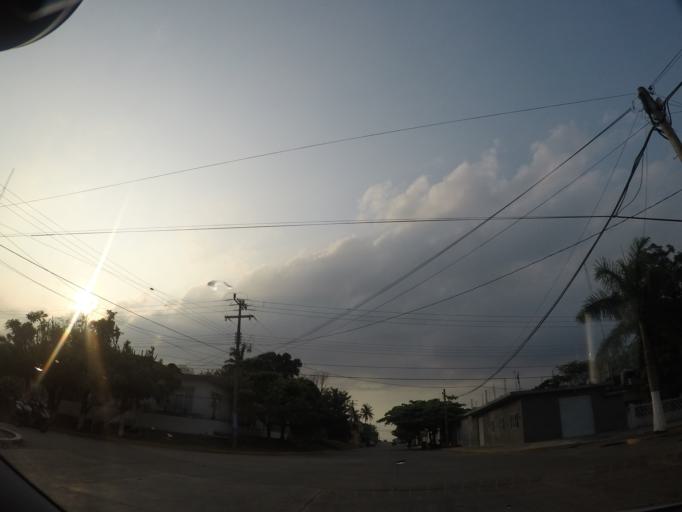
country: MX
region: Oaxaca
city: Matias Romero
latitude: 16.8729
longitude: -95.0429
